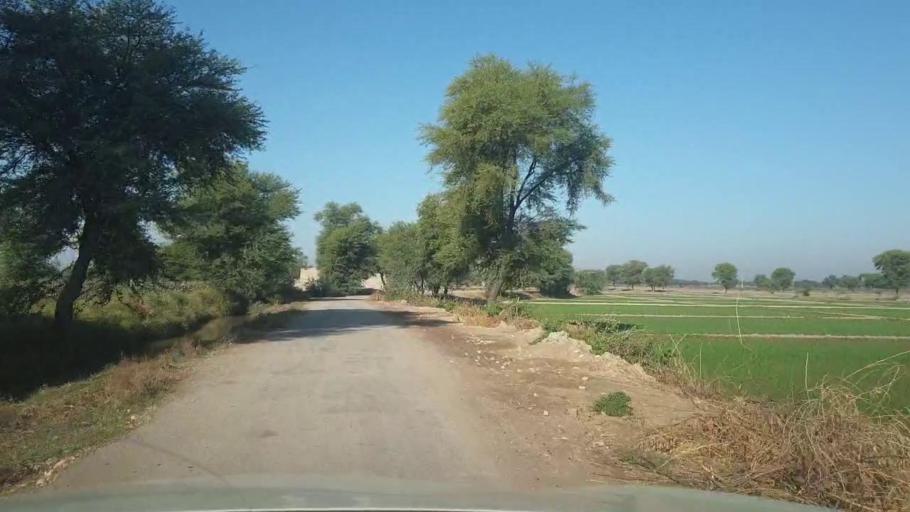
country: PK
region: Sindh
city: Bhan
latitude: 26.5464
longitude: 67.6717
